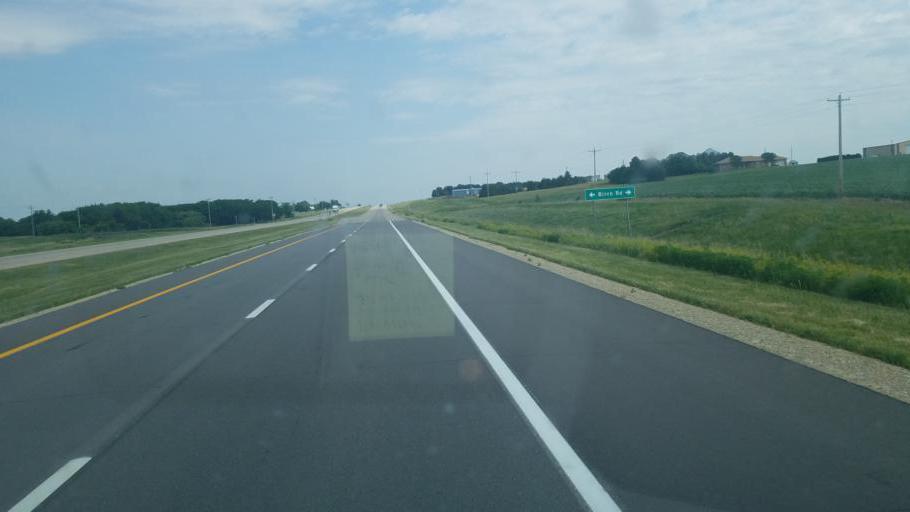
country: US
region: Kansas
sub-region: Republic County
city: Belleville
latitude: 39.9843
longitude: -97.6128
